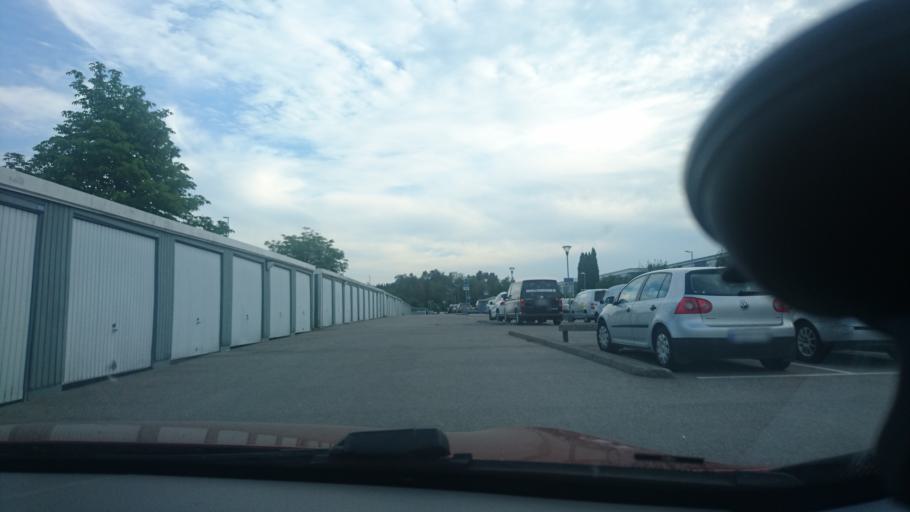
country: SE
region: Stockholm
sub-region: Upplands Vasby Kommun
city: Upplands Vaesby
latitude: 59.5071
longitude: 17.9173
